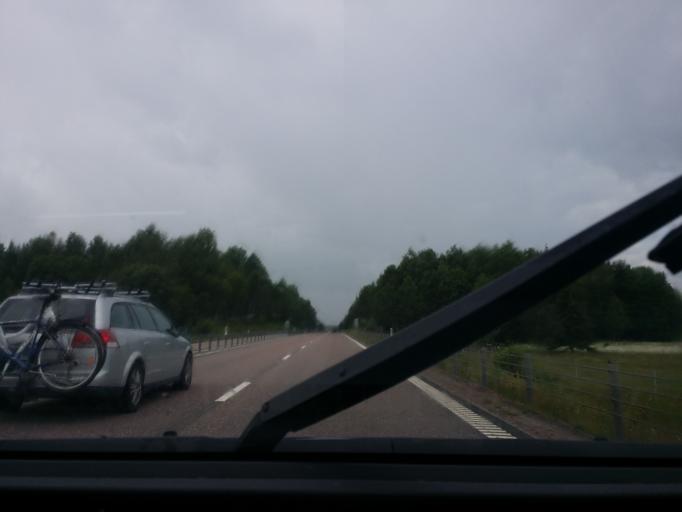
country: SE
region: Vaestmanland
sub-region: Hallstahammars Kommun
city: Kolback
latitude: 59.5836
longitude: 16.2837
